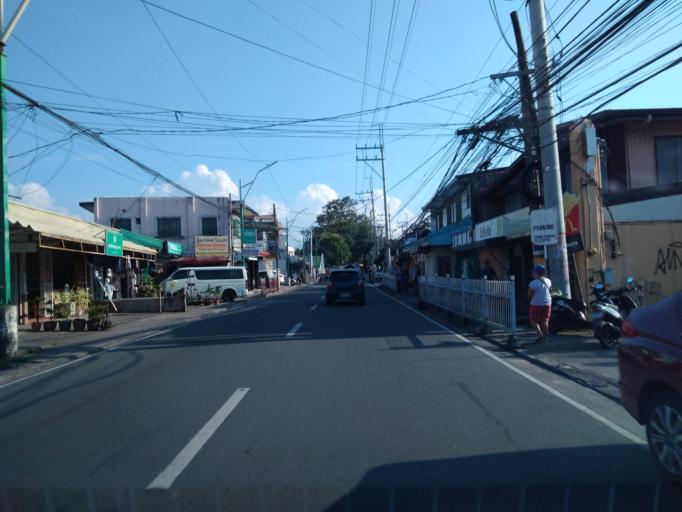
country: PH
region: Calabarzon
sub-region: Province of Laguna
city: Los Banos
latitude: 14.1754
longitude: 121.2430
